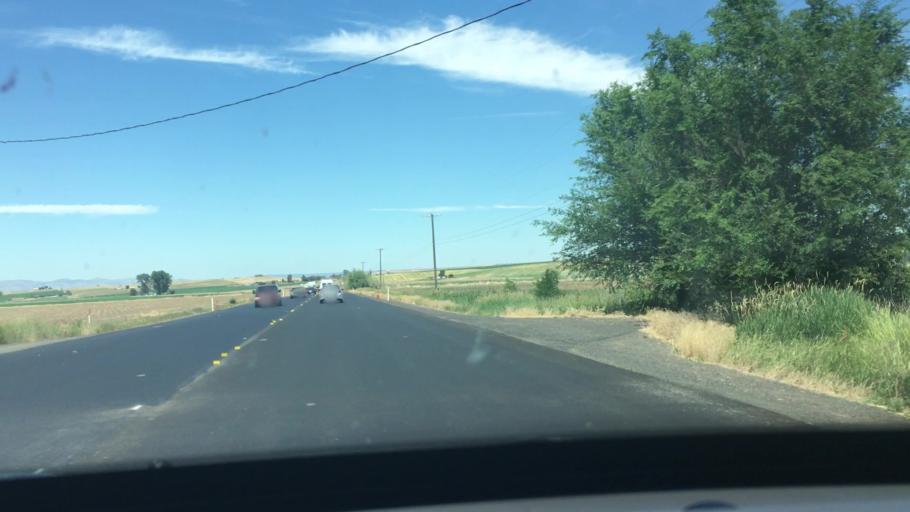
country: US
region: Oregon
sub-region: Jefferson County
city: Culver
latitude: 44.5095
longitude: -121.1865
